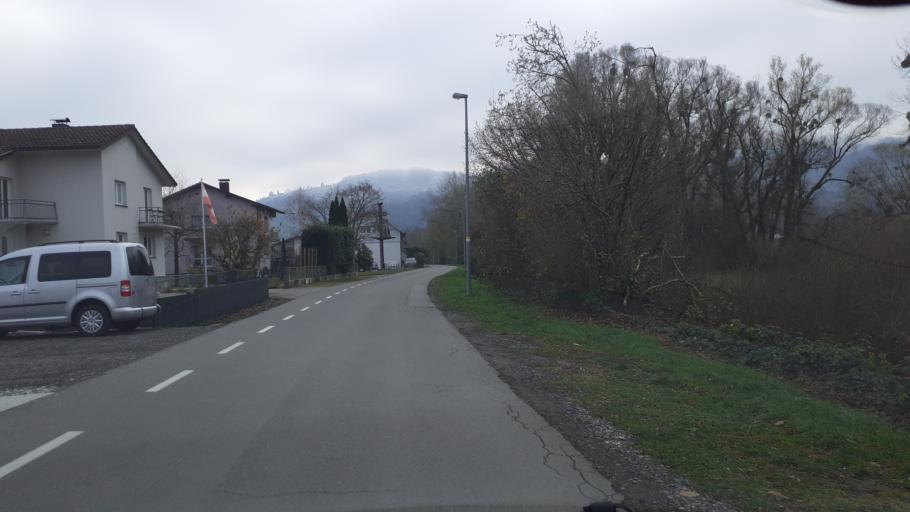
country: CH
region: Saint Gallen
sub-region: Wahlkreis Rheintal
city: Rheineck
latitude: 47.4755
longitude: 9.5886
